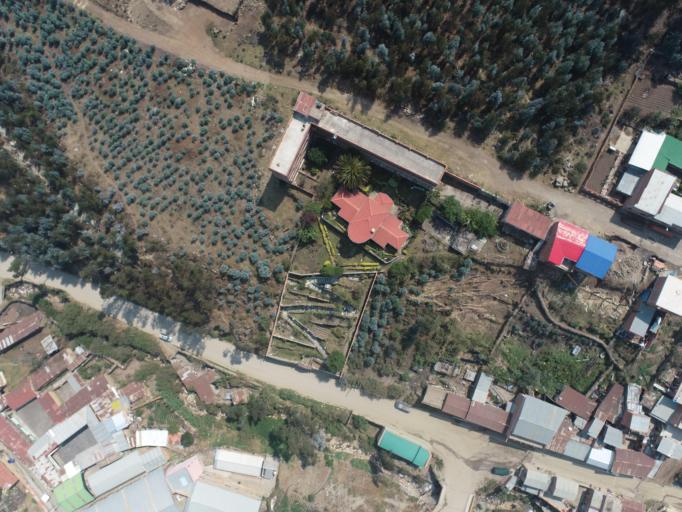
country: BO
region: La Paz
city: Quime
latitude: -16.9818
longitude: -67.2144
